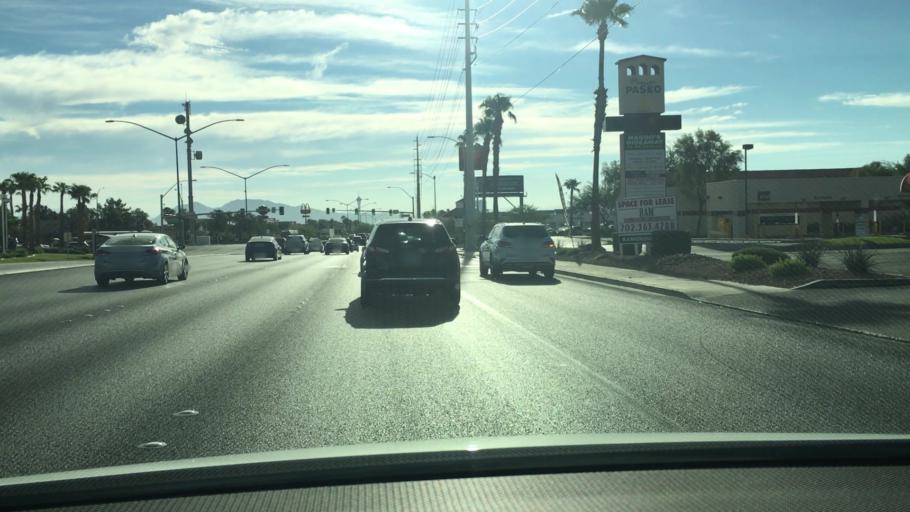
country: US
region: Nevada
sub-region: Clark County
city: Spring Valley
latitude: 36.1440
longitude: -115.2448
